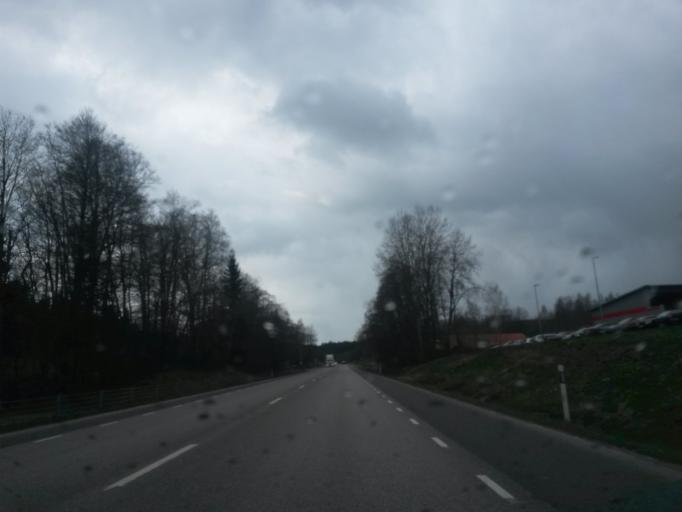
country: SE
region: Vaestra Goetaland
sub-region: Skovde Kommun
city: Skoevde
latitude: 58.3875
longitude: 13.7960
